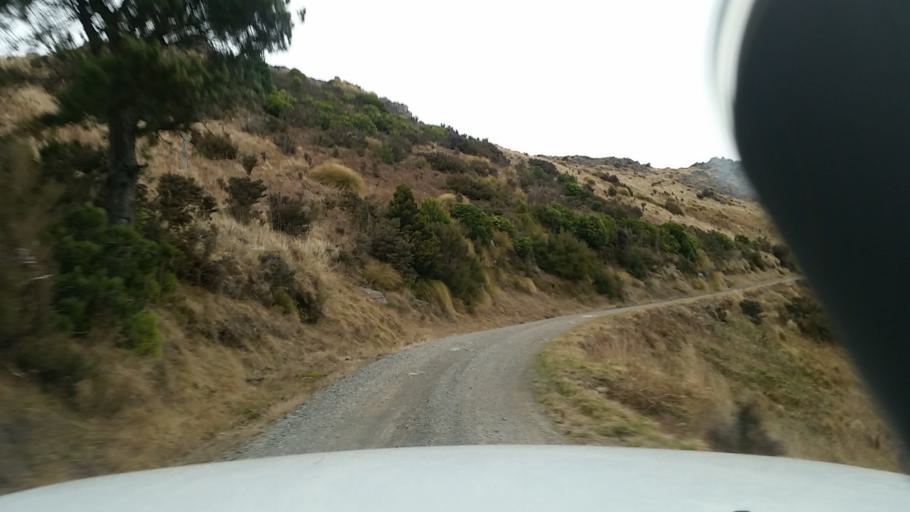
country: NZ
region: Canterbury
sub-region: Christchurch City
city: Christchurch
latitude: -43.8111
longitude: 172.8281
